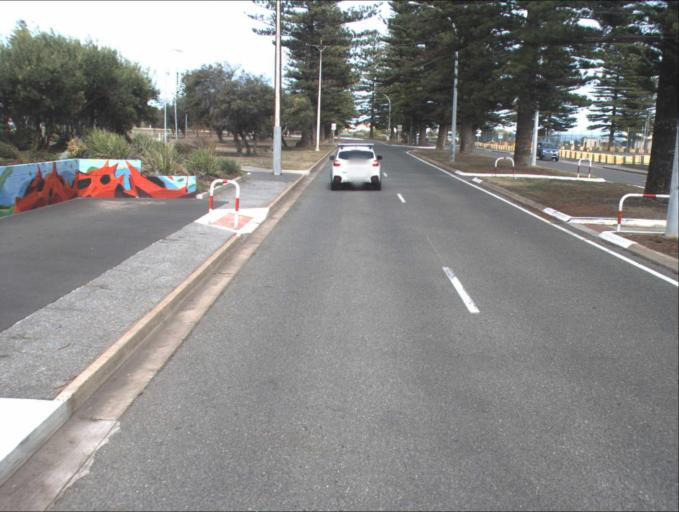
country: AU
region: South Australia
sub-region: Port Adelaide Enfield
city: Birkenhead
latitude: -34.7785
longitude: 138.4838
